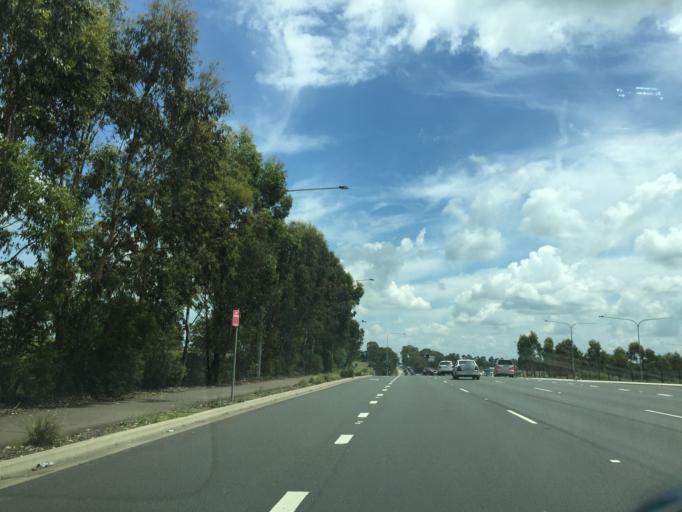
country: AU
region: New South Wales
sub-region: Blacktown
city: Rouse Hill
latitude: -33.6921
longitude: 150.9235
